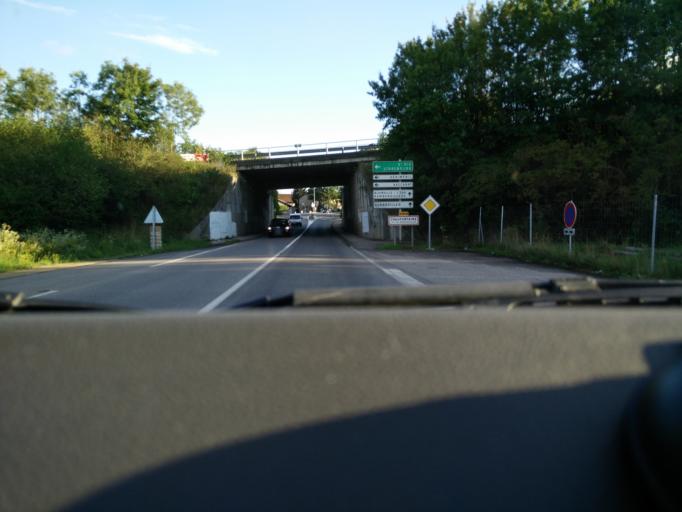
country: FR
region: Lorraine
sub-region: Departement de Meurthe-et-Moselle
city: Luneville
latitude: 48.5765
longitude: 6.4817
